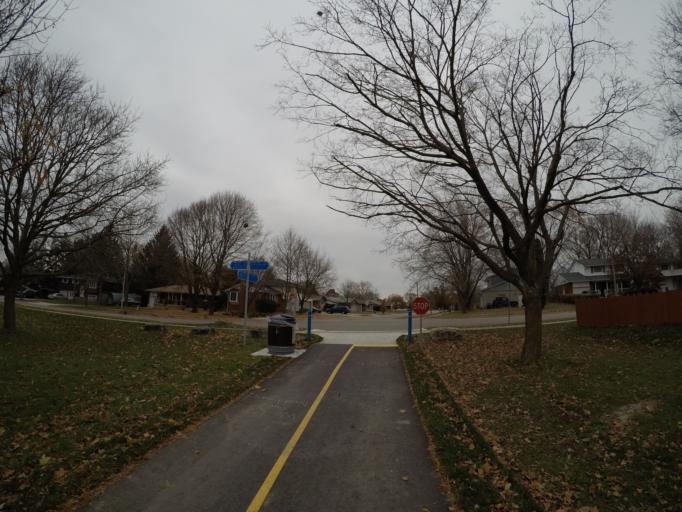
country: CA
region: Ontario
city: Waterloo
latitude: 43.4761
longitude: -80.5135
